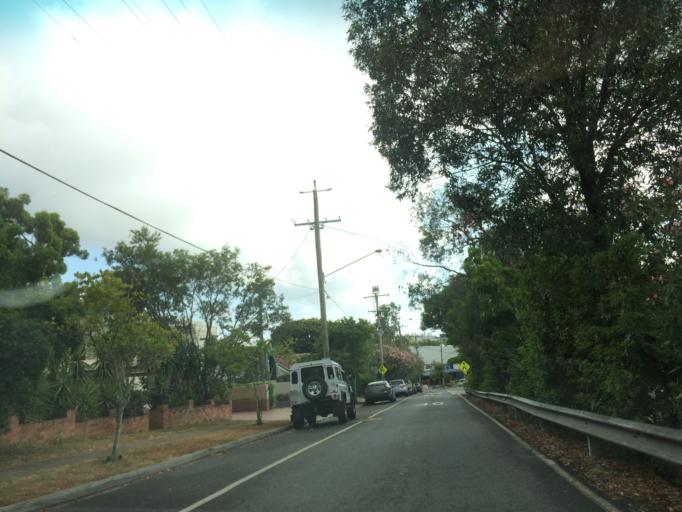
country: AU
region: Queensland
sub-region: Brisbane
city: Yeronga
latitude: -27.5033
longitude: 153.0048
